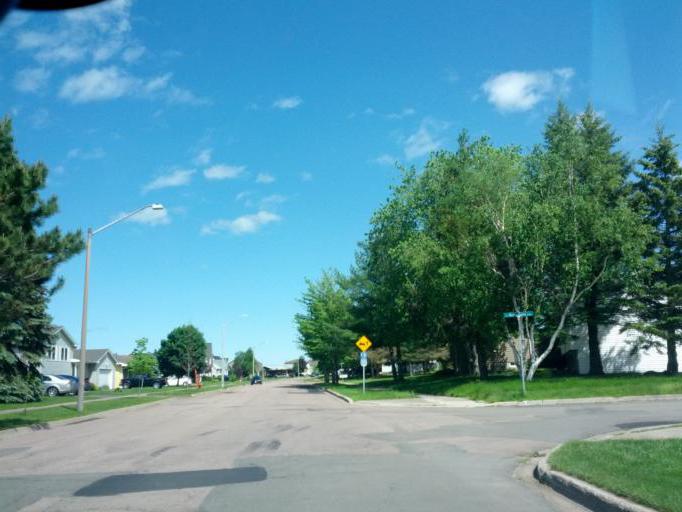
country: CA
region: New Brunswick
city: Moncton
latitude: 46.1252
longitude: -64.8500
